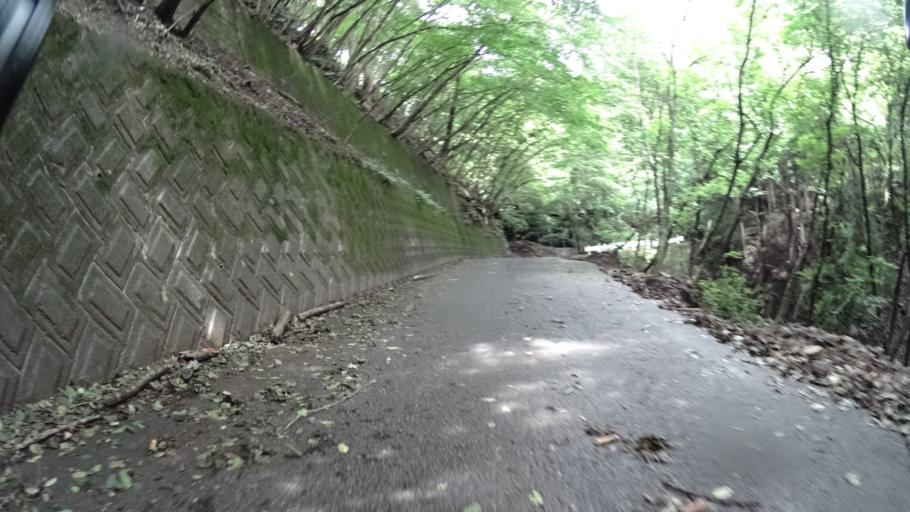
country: JP
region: Saitama
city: Chichibu
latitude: 35.8905
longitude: 139.1359
